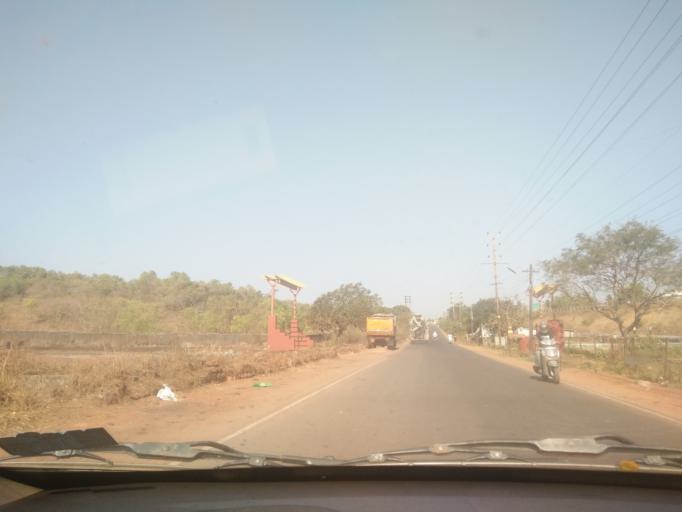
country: IN
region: Goa
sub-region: South Goa
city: Chicalim
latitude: 15.3855
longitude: 73.8666
